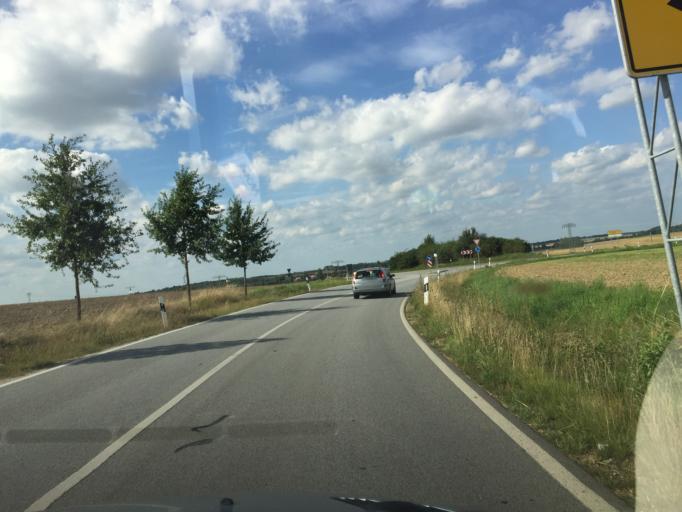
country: DE
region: Saxony
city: Kubschutz
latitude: 51.1802
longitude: 14.4857
